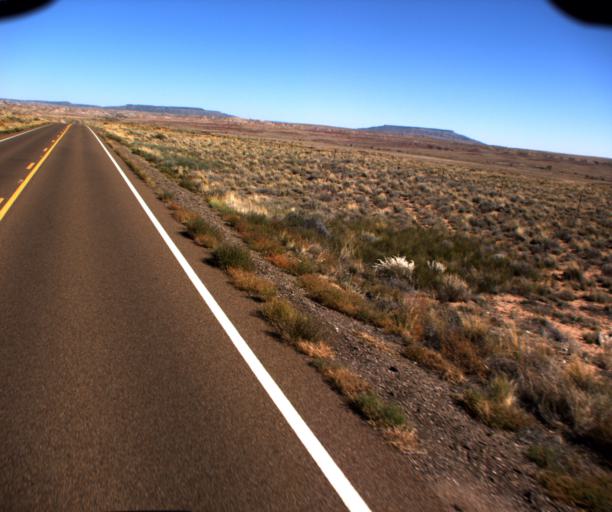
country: US
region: Arizona
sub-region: Navajo County
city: Joseph City
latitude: 35.1584
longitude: -110.4615
